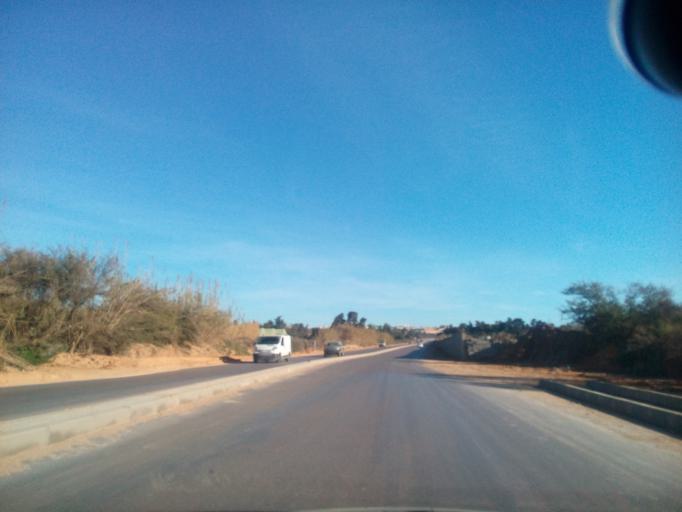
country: DZ
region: Mostaganem
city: Mostaganem
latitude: 35.9192
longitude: 0.1263
